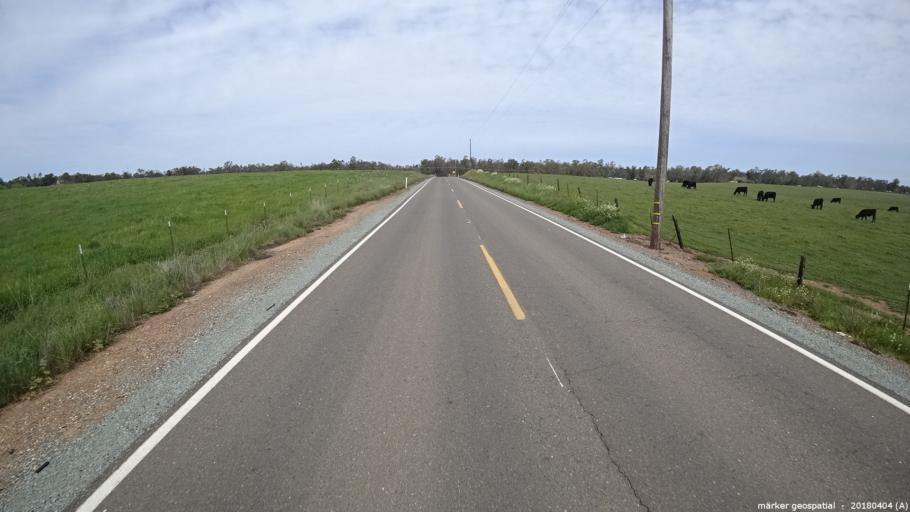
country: US
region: California
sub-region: Sacramento County
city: Clay
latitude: 38.2891
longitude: -121.1713
